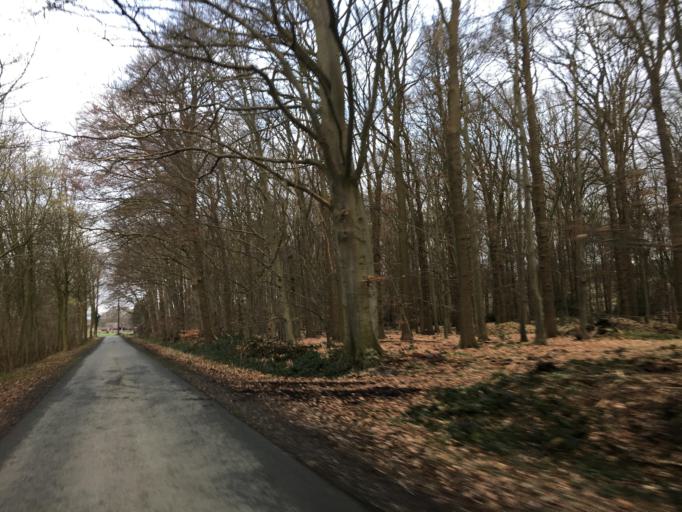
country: DE
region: North Rhine-Westphalia
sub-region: Regierungsbezirk Munster
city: Senden
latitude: 51.9199
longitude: 7.4930
